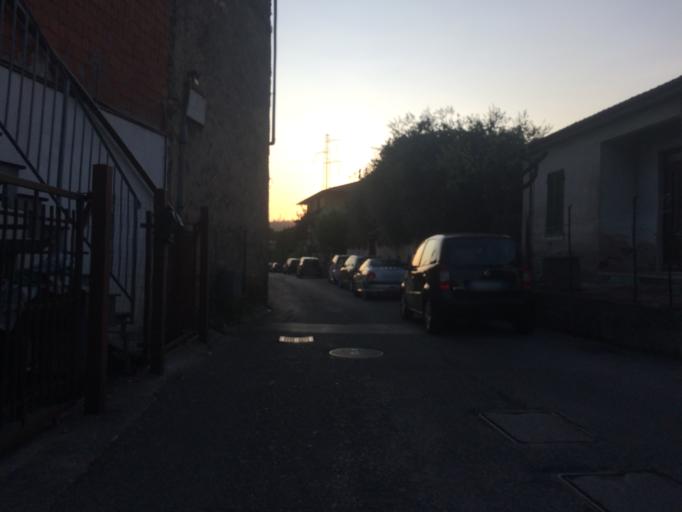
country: IT
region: Tuscany
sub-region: Provincia di Massa-Carrara
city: Massa
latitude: 44.0397
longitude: 10.1183
